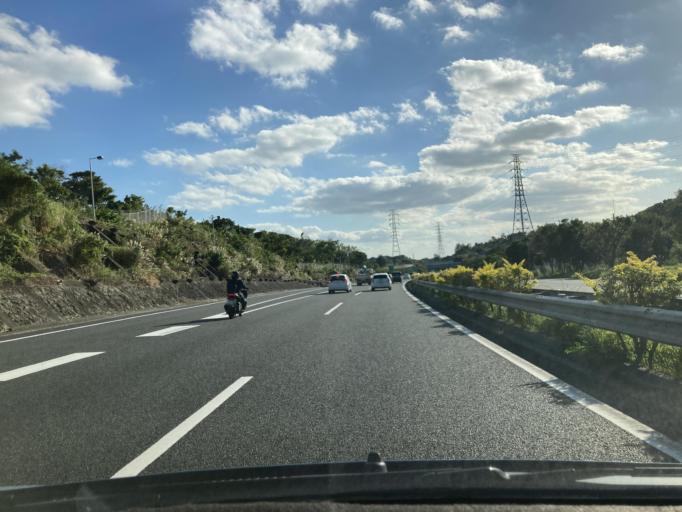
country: JP
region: Okinawa
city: Okinawa
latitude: 26.3189
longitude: 127.7898
